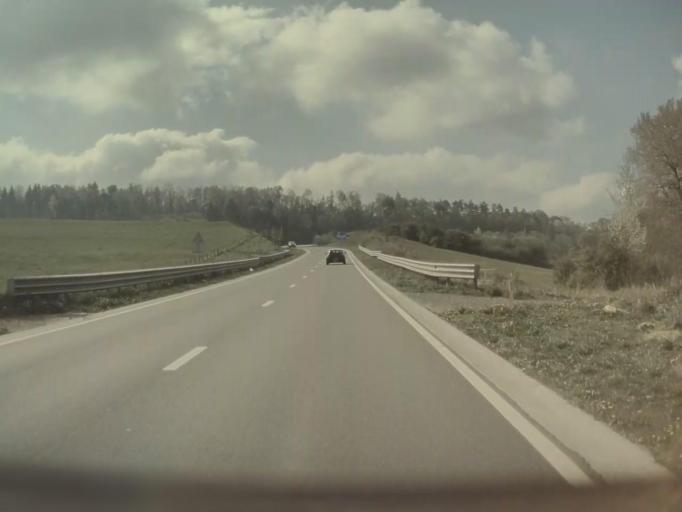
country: BE
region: Wallonia
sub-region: Province du Luxembourg
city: Marche-en-Famenne
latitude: 50.2196
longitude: 5.3155
